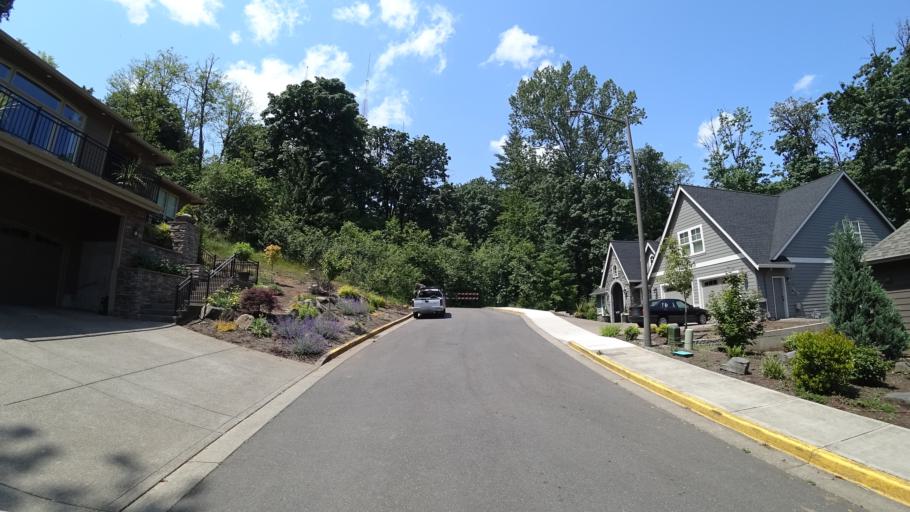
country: US
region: Oregon
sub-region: Clackamas County
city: Happy Valley
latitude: 45.4536
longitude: -122.5443
